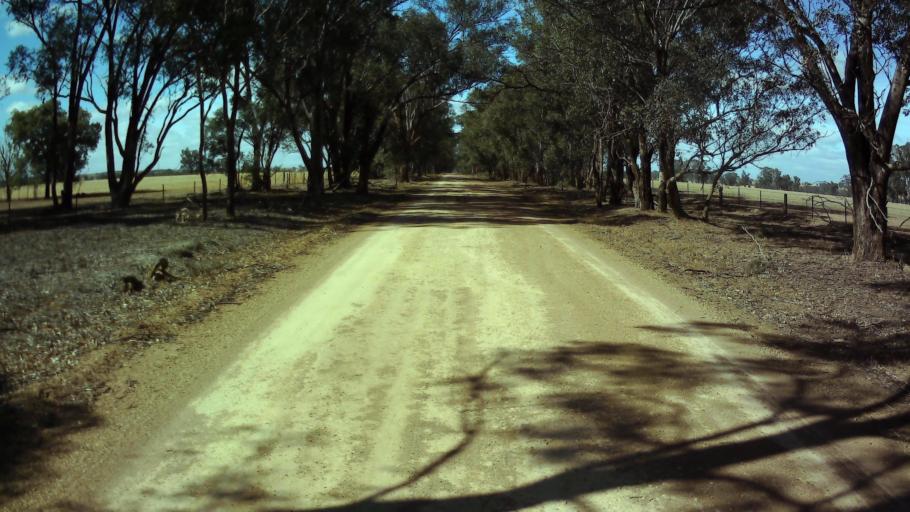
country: AU
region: New South Wales
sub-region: Weddin
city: Grenfell
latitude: -34.0464
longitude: 148.3147
